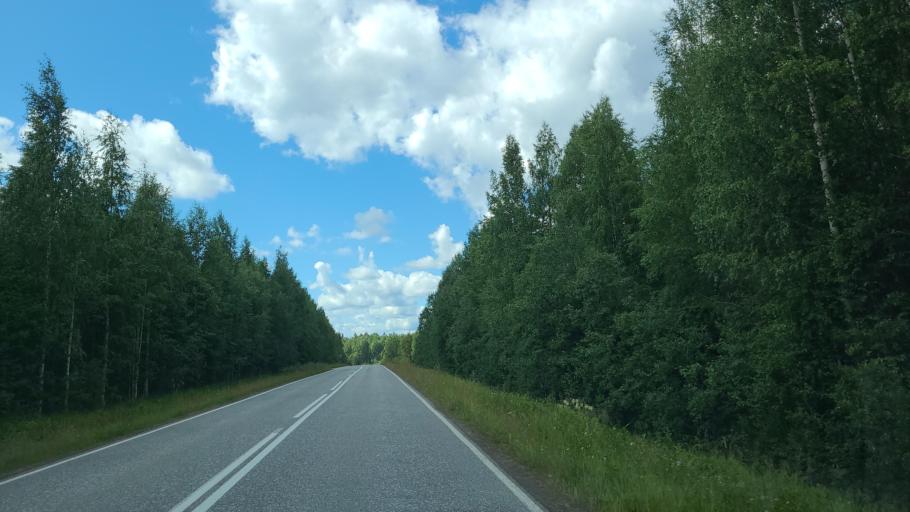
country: FI
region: Northern Savo
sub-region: Koillis-Savo
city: Kaavi
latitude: 62.9769
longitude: 28.7888
